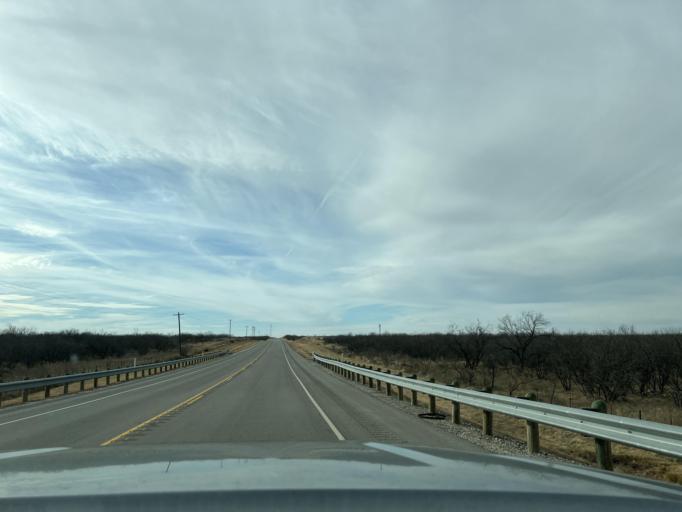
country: US
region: Texas
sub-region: Jones County
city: Anson
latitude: 32.7506
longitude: -99.7012
